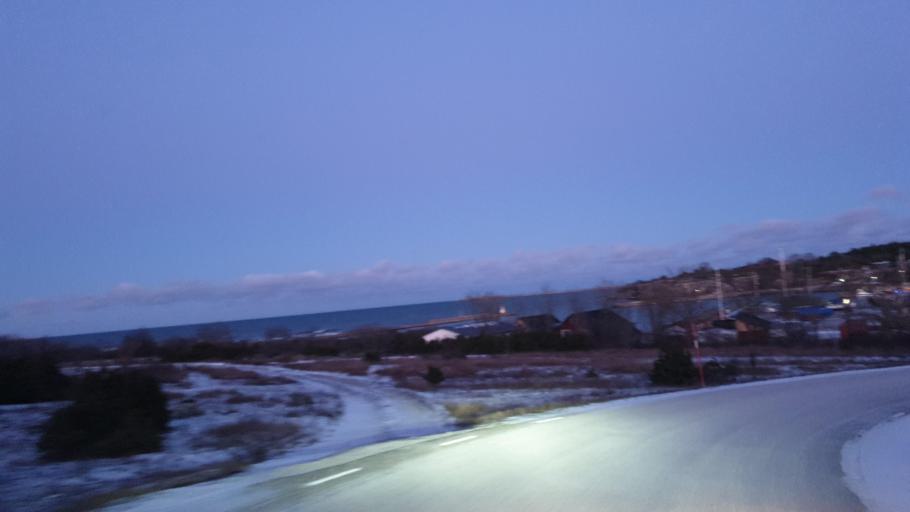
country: SE
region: Gotland
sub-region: Gotland
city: Slite
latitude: 57.4219
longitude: 18.9103
